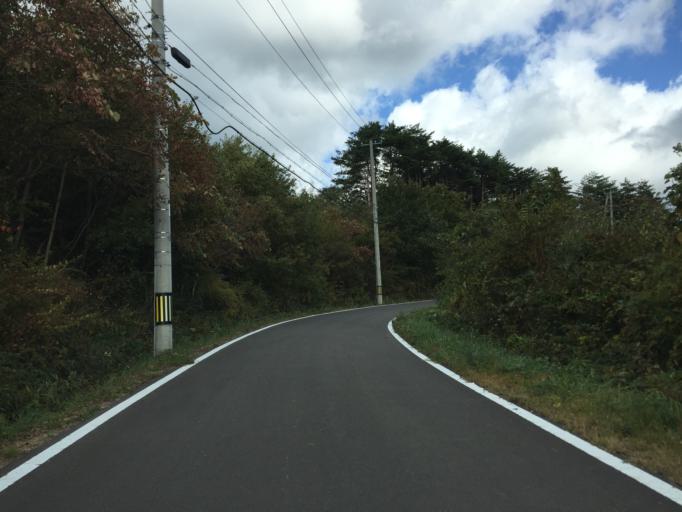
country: JP
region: Miyagi
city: Marumori
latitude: 37.8126
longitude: 140.7741
